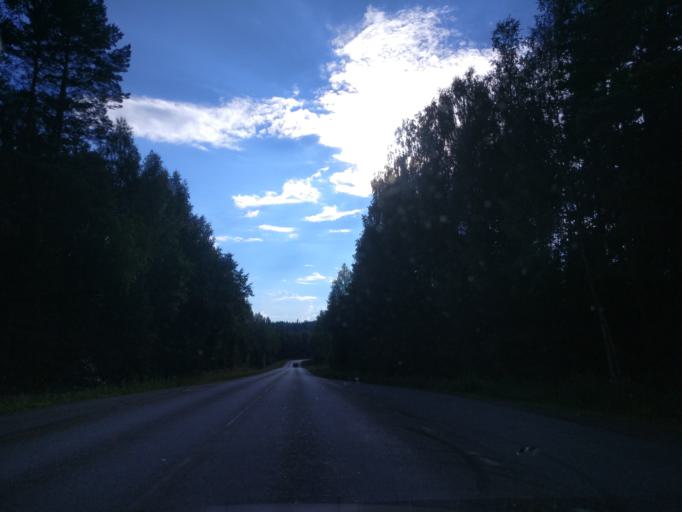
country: SE
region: Dalarna
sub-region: Ludvika Kommun
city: Ludvika
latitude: 60.2858
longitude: 15.1512
